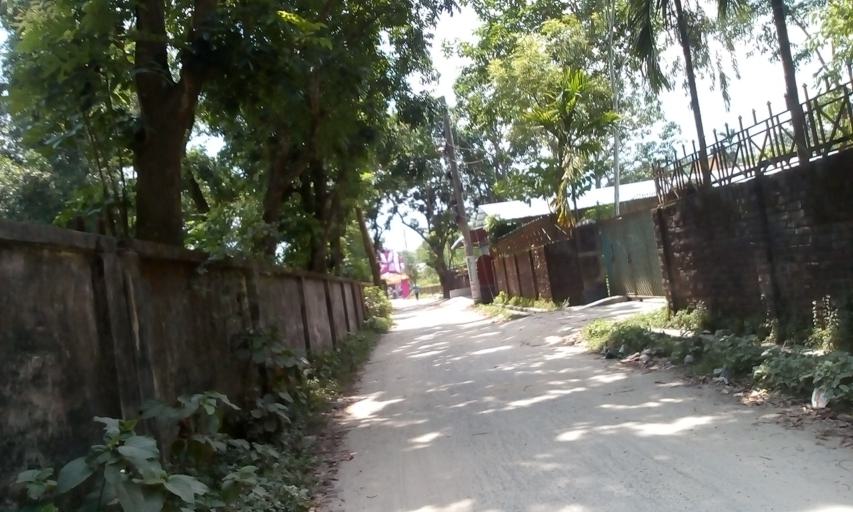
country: IN
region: West Bengal
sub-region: Dakshin Dinajpur
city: Balurghat
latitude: 25.3810
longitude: 88.9891
